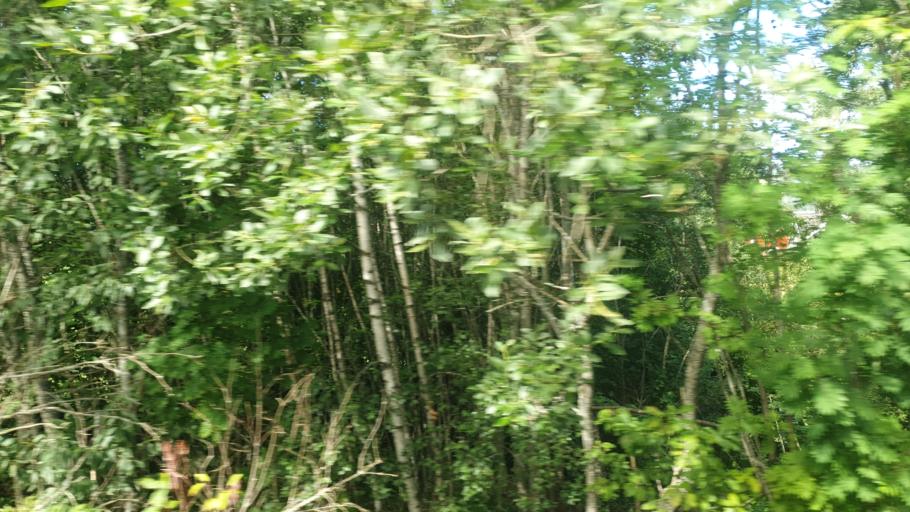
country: NO
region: Sor-Trondelag
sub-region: Orkdal
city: Orkanger
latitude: 63.2704
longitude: 9.8188
